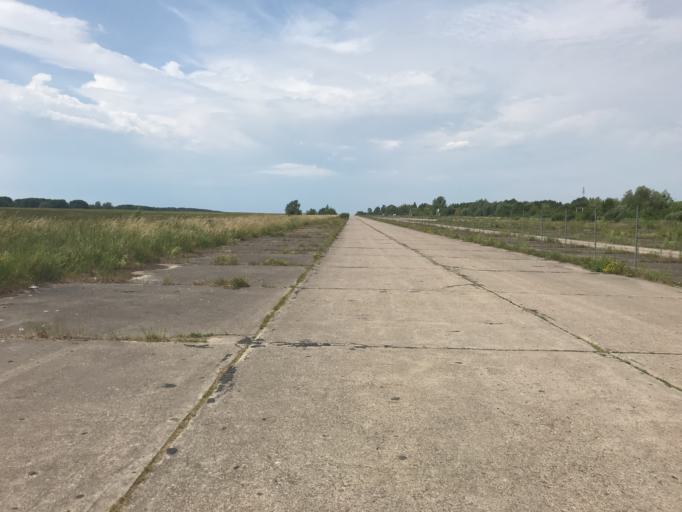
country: PL
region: West Pomeranian Voivodeship
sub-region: Powiat gryfinski
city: Chojna
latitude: 52.9423
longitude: 14.4338
